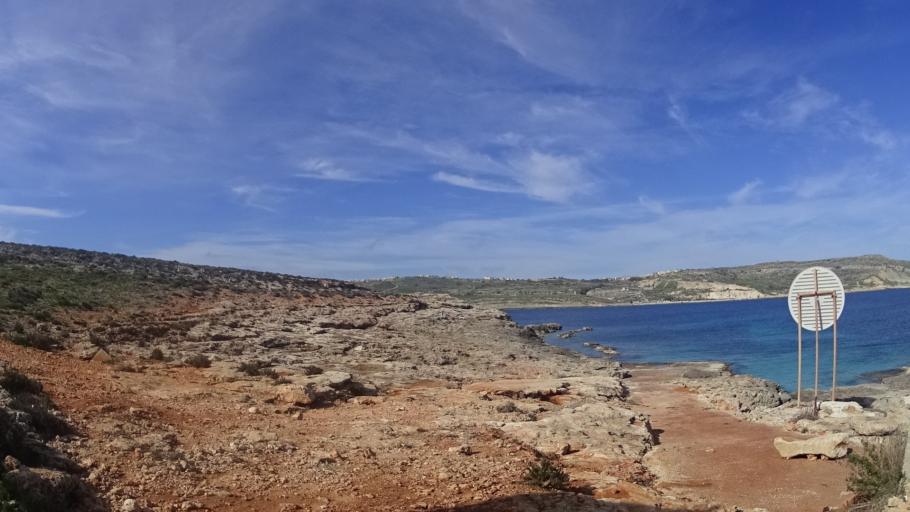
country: MT
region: Il-Qala
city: Qala
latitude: 36.0173
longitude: 14.3255
